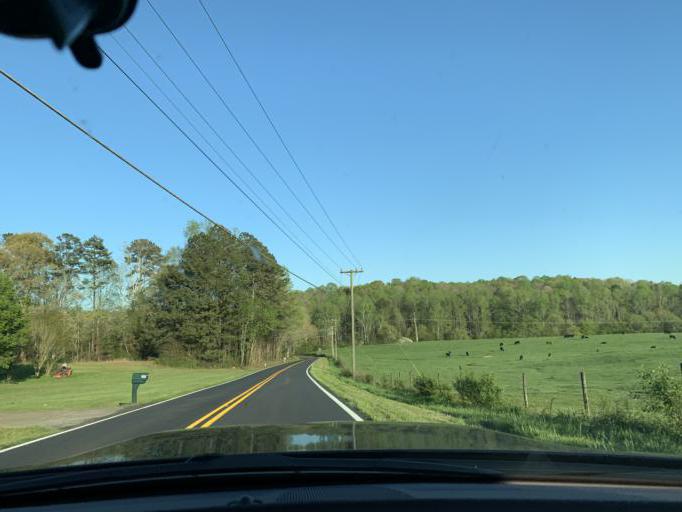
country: US
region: Georgia
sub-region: Forsyth County
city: Cumming
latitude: 34.2590
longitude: -84.2114
